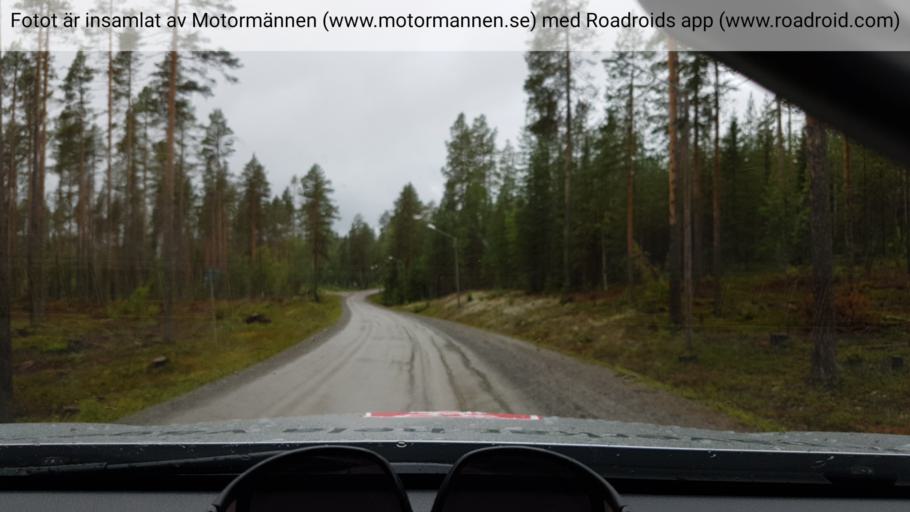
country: SE
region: Vaesterbotten
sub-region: Lycksele Kommun
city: Soderfors
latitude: 64.9667
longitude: 17.5934
